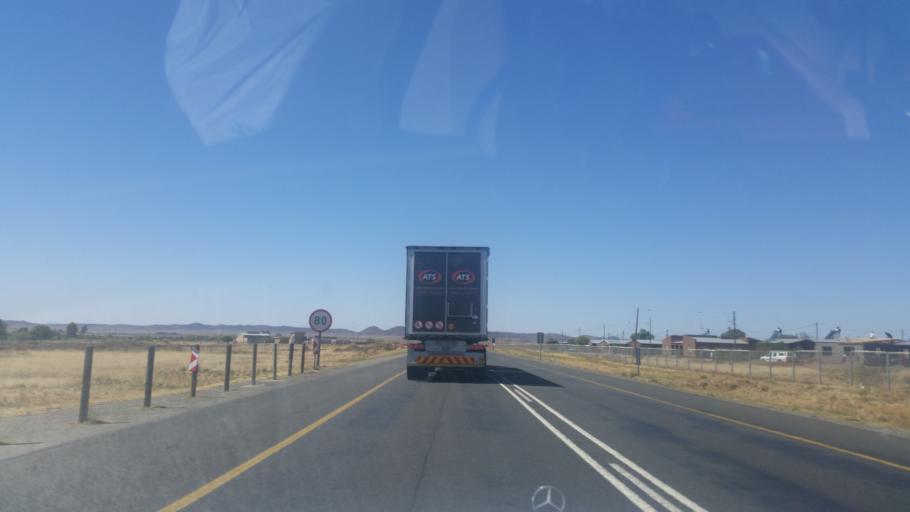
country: ZA
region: Northern Cape
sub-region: Pixley ka Seme District Municipality
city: Colesberg
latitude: -30.7073
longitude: 25.1106
